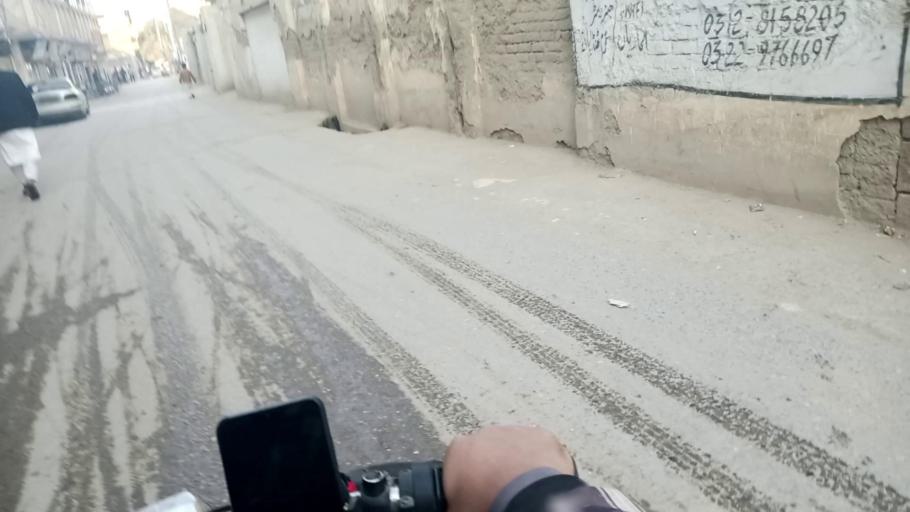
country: PK
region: Khyber Pakhtunkhwa
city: Peshawar
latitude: 34.0044
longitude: 71.4726
